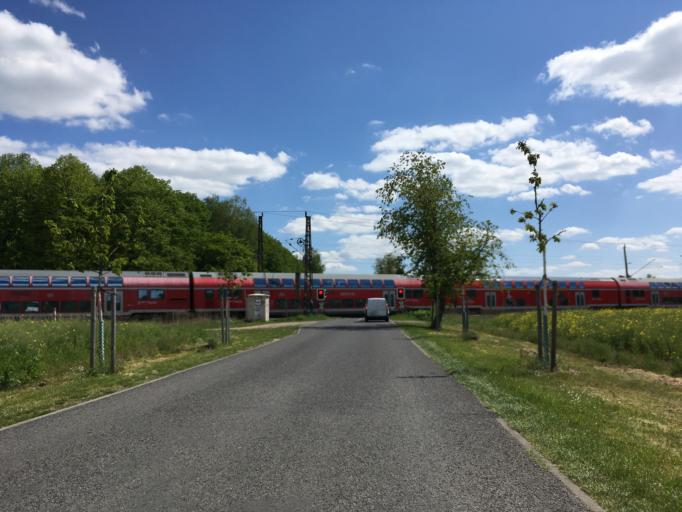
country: DE
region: Brandenburg
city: Biesenthal
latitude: 52.7395
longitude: 13.6574
